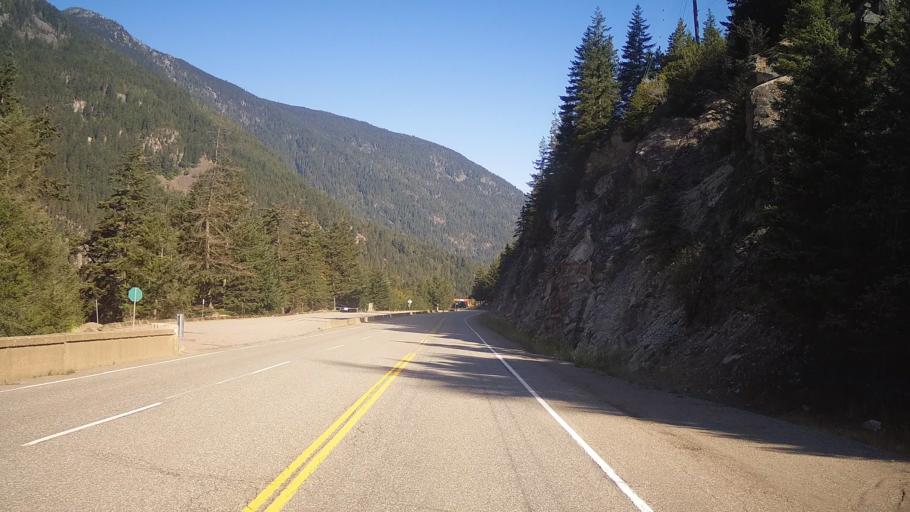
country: CA
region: British Columbia
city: Hope
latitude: 49.7765
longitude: -121.4407
